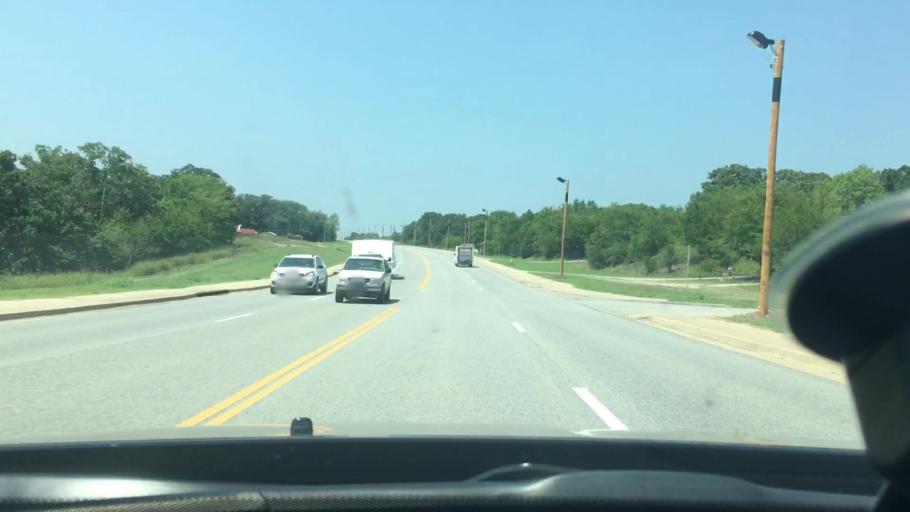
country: US
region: Oklahoma
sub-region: Atoka County
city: Atoka
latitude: 34.3744
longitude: -96.1152
